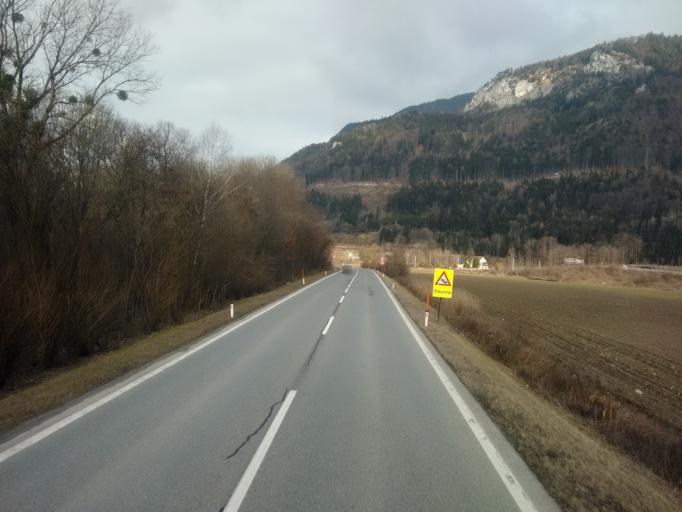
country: AT
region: Styria
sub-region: Politischer Bezirk Liezen
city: Stainach
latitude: 47.5259
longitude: 14.0995
